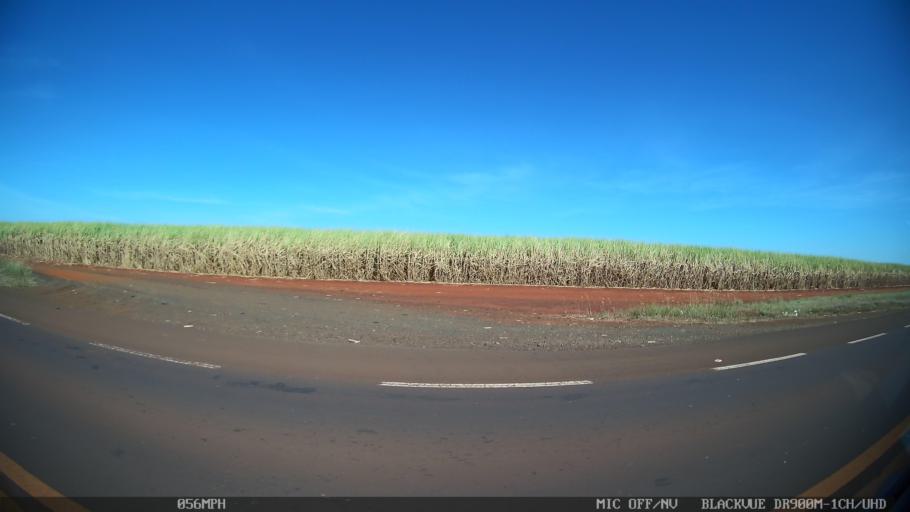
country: BR
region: Sao Paulo
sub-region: Guaira
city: Guaira
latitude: -20.4446
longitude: -48.2675
